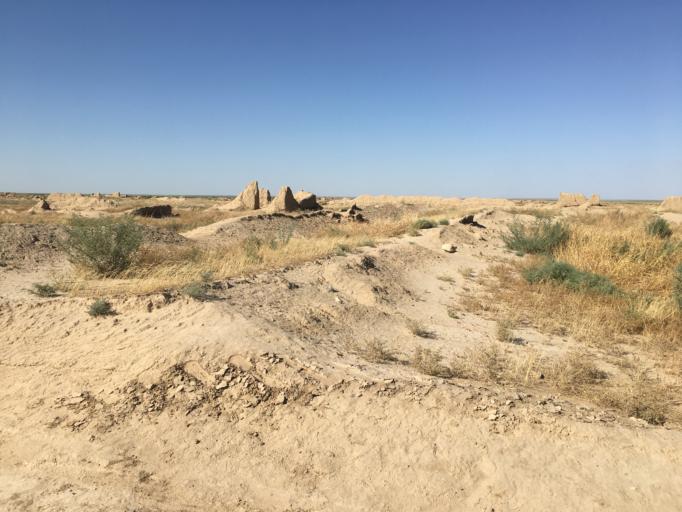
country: TM
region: Ahal
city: Tejen
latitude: 36.9804
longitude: 60.2506
